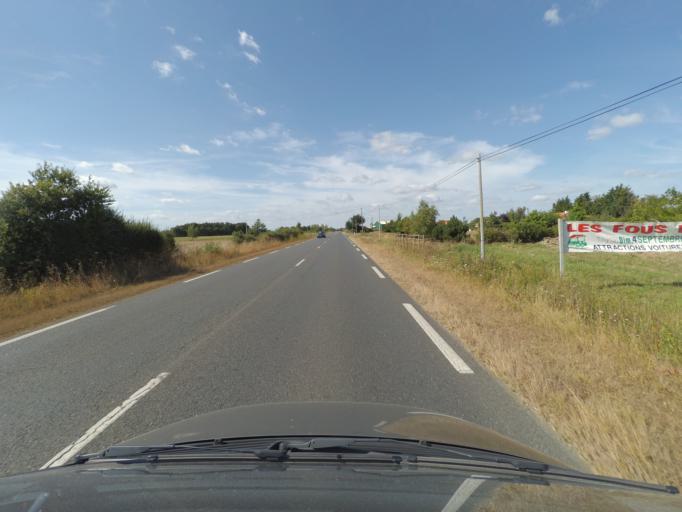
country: FR
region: Pays de la Loire
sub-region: Departement de la Loire-Atlantique
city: Les Sorinieres
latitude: 47.1052
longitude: -1.5364
